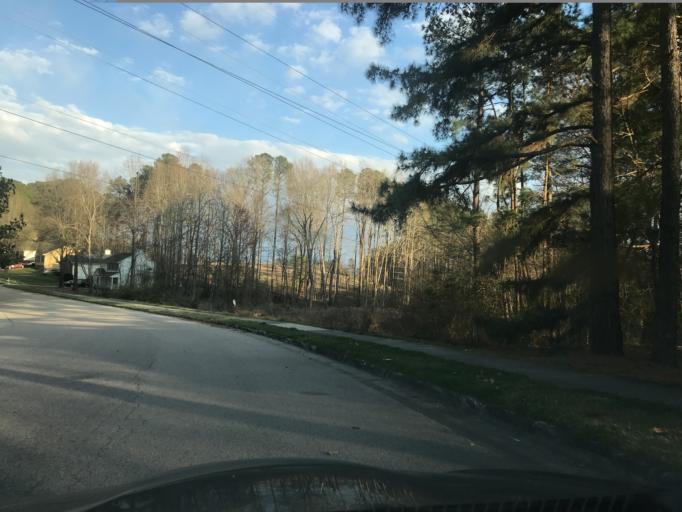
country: US
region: North Carolina
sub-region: Wake County
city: Raleigh
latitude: 35.8500
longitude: -78.5697
